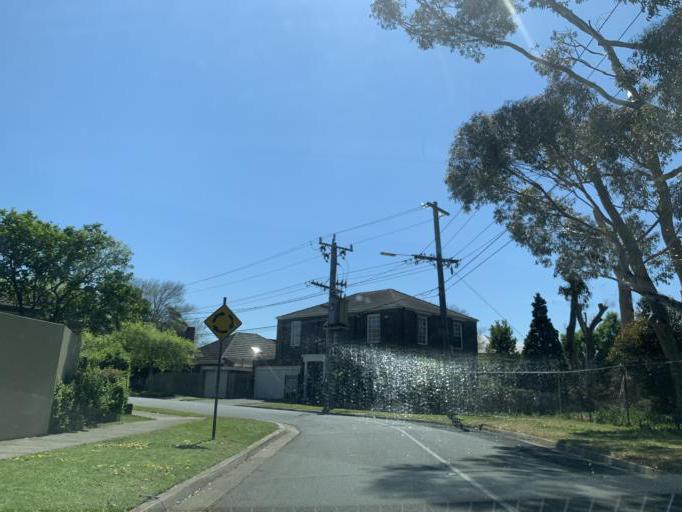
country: AU
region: Victoria
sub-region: Bayside
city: Hampton
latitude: -37.9271
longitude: 145.0137
